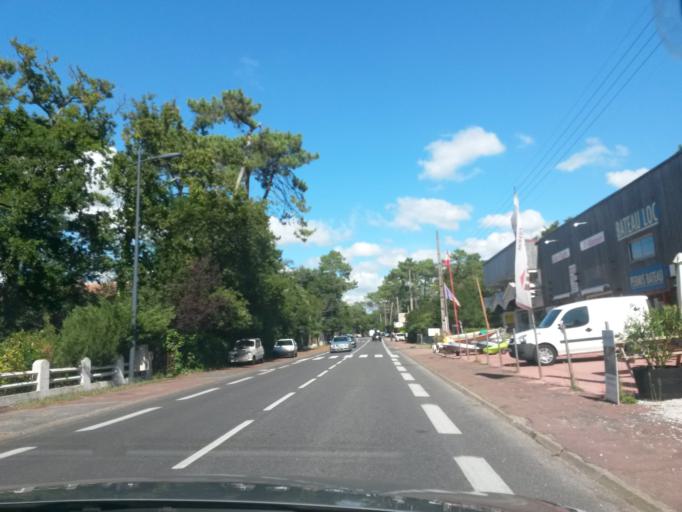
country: FR
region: Aquitaine
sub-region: Departement de la Gironde
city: Arcachon
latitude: 44.7141
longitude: -1.2156
